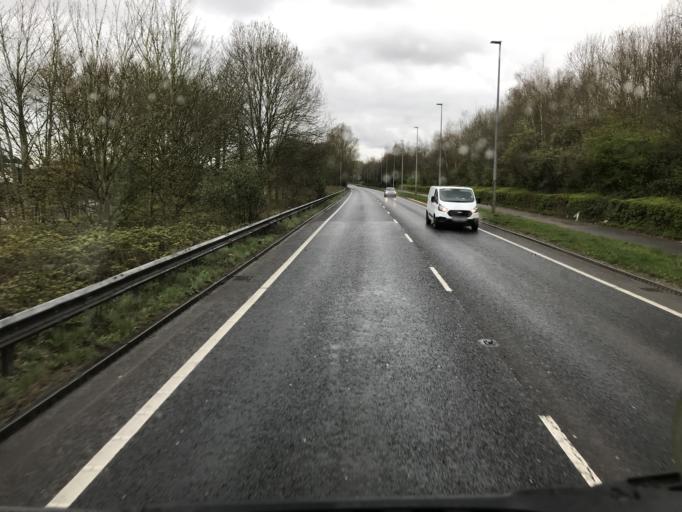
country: GB
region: England
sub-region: City and Borough of Salford
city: Irlam
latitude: 53.4494
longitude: -2.4080
